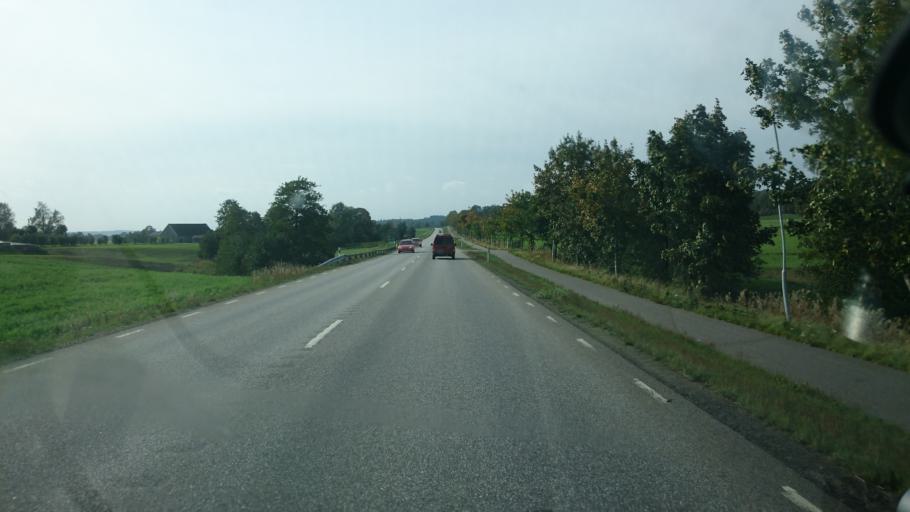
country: SE
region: Vaestra Goetaland
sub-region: Alingsas Kommun
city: Sollebrunn
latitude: 58.0994
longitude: 12.5083
